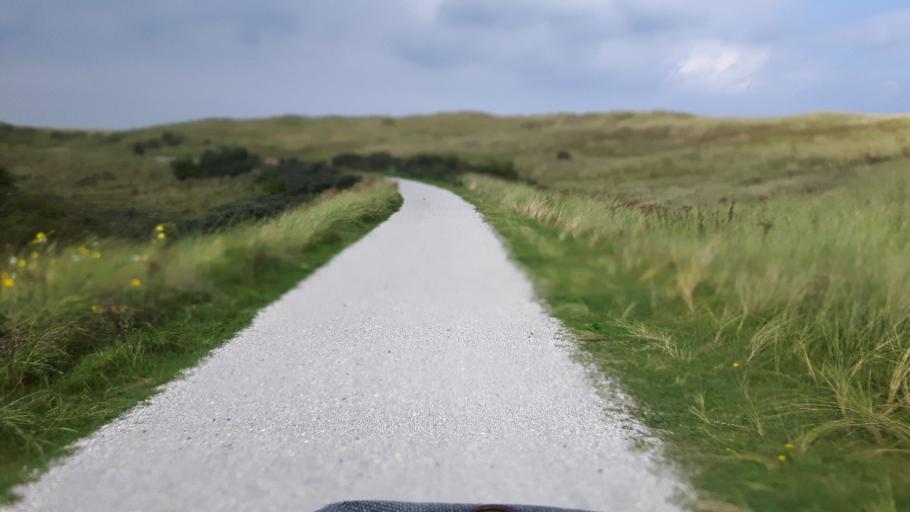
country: NL
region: Friesland
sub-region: Gemeente Dongeradeel
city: Holwerd
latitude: 53.4593
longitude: 5.9019
